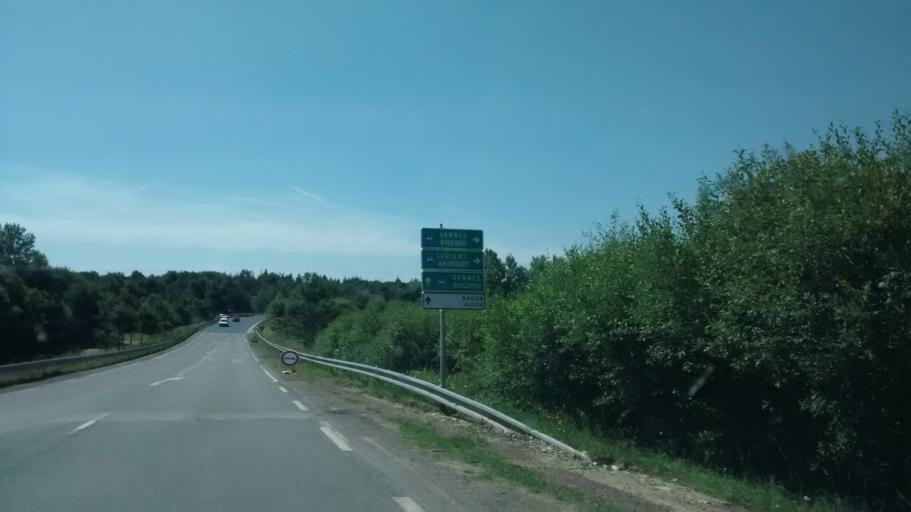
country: FR
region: Brittany
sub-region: Departement du Morbihan
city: Campeneac
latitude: 47.9418
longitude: -2.2854
